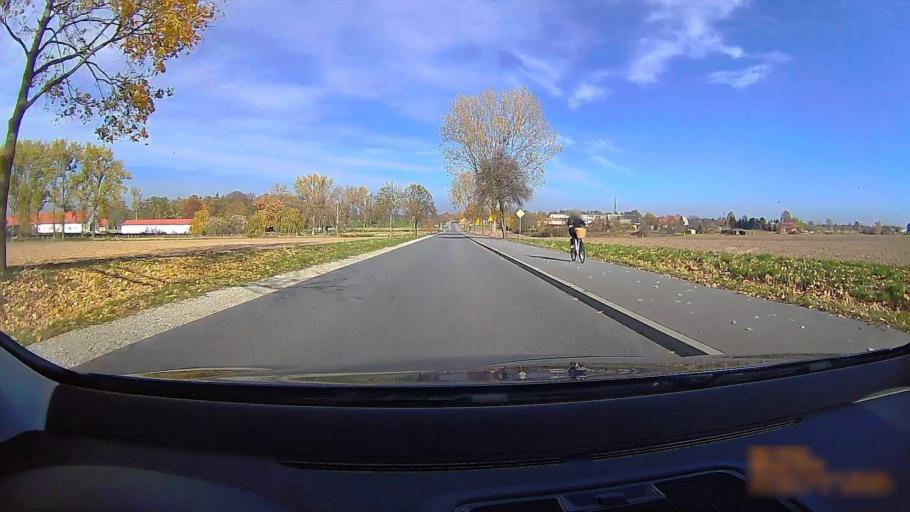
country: PL
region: Greater Poland Voivodeship
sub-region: Powiat kepinski
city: Kepno
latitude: 51.3423
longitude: 18.0229
